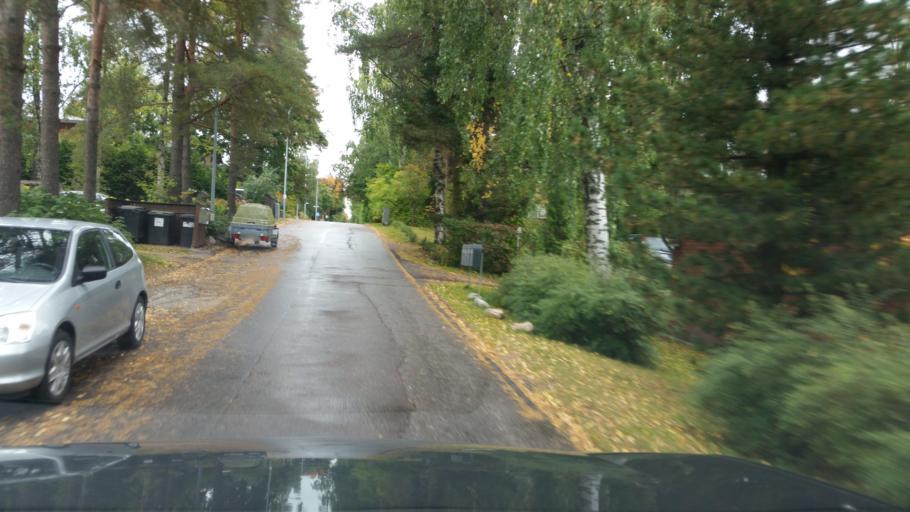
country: FI
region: Uusimaa
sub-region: Helsinki
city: Helsinki
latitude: 60.2381
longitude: 24.9203
